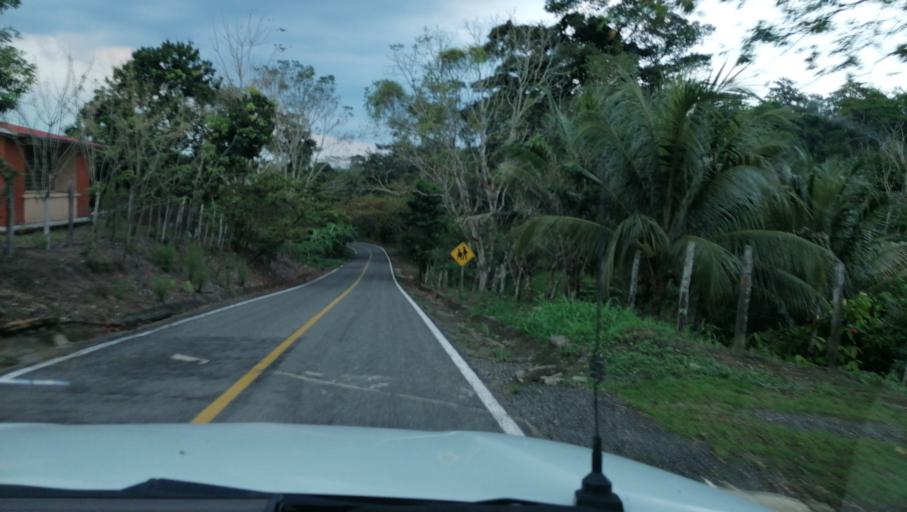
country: MX
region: Chiapas
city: Pichucalco
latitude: 17.5214
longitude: -93.1543
